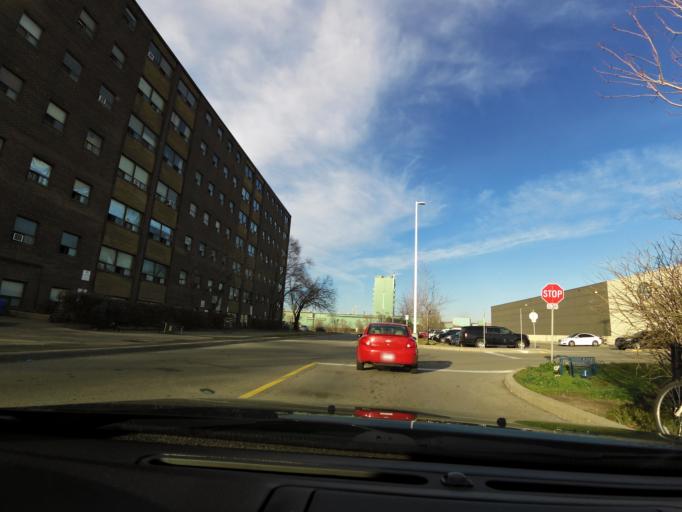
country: CA
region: Ontario
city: Hamilton
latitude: 43.2530
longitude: -79.8135
